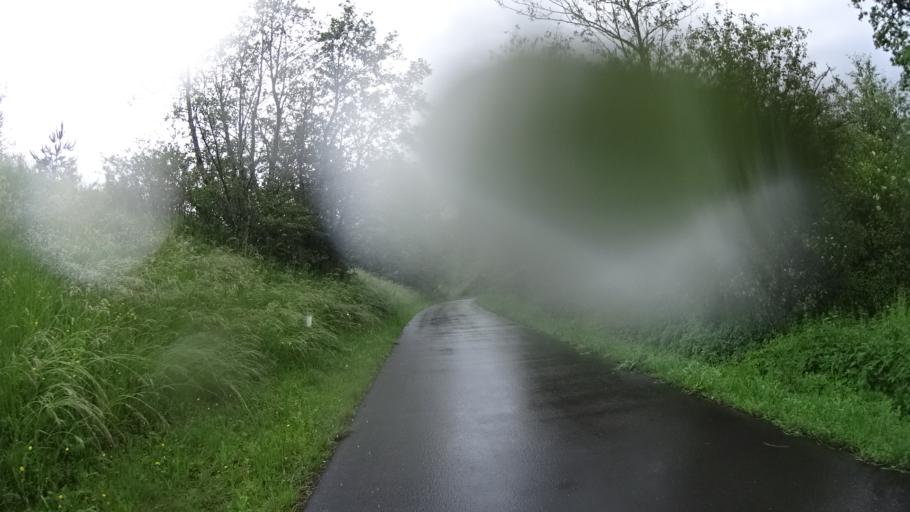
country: LI
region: Ruggell
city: Ruggell
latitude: 47.2597
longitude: 9.5299
